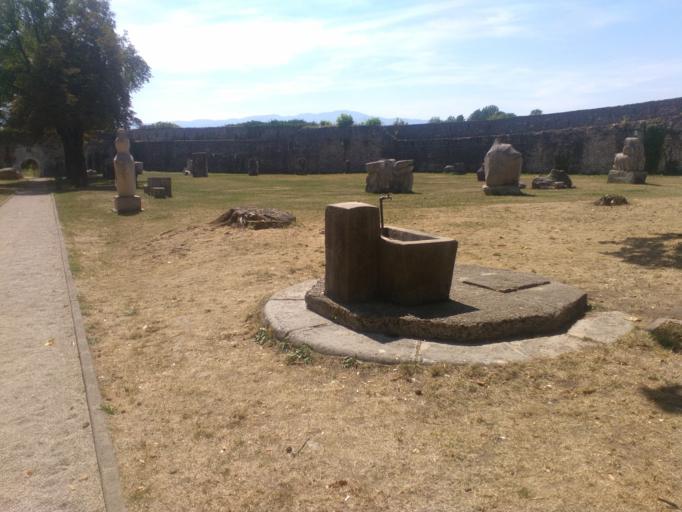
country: BA
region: Federation of Bosnia and Herzegovina
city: Ostrozac
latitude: 44.9053
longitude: 15.9371
